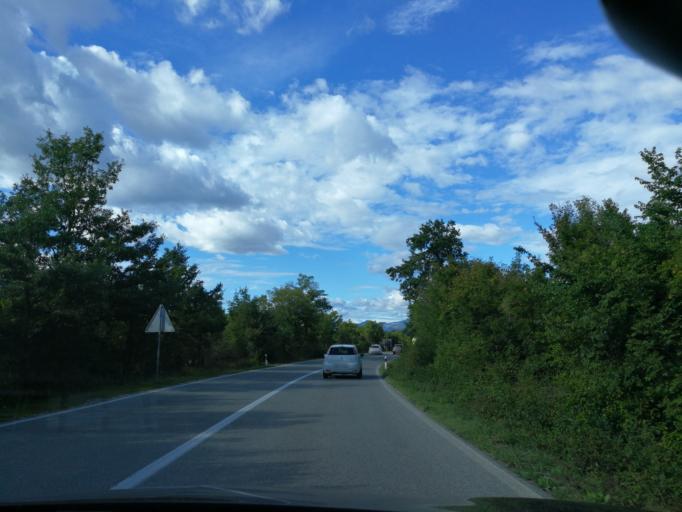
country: HR
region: Primorsko-Goranska
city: Omisalj
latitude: 45.1810
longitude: 14.5561
